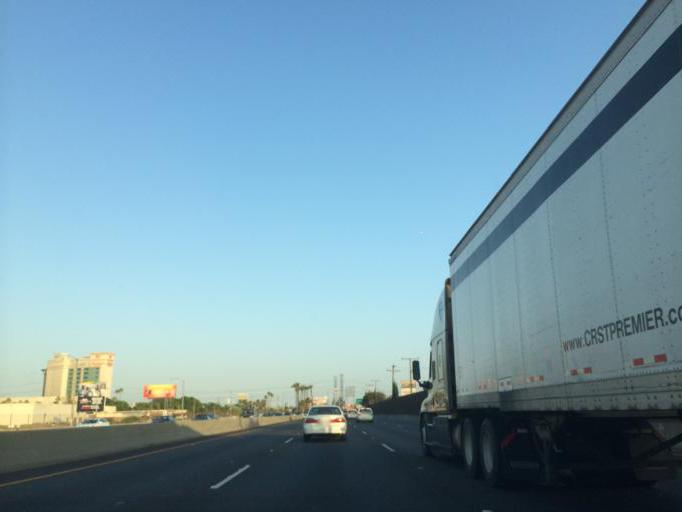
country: US
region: California
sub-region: Los Angeles County
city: Commerce
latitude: 34.0009
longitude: -118.1496
